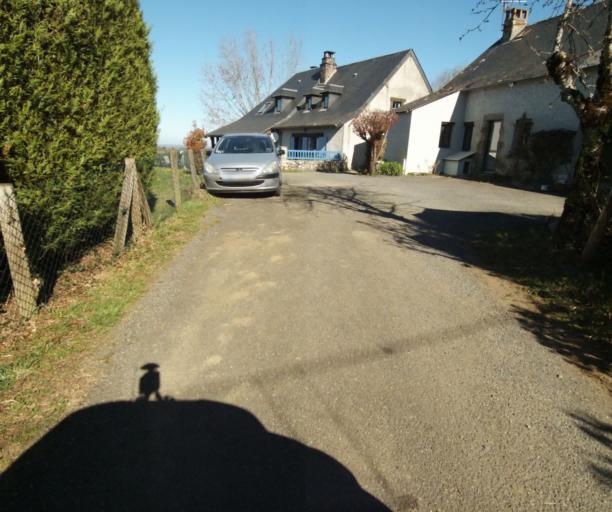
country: FR
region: Limousin
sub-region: Departement de la Correze
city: Chamboulive
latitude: 45.4077
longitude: 1.7043
